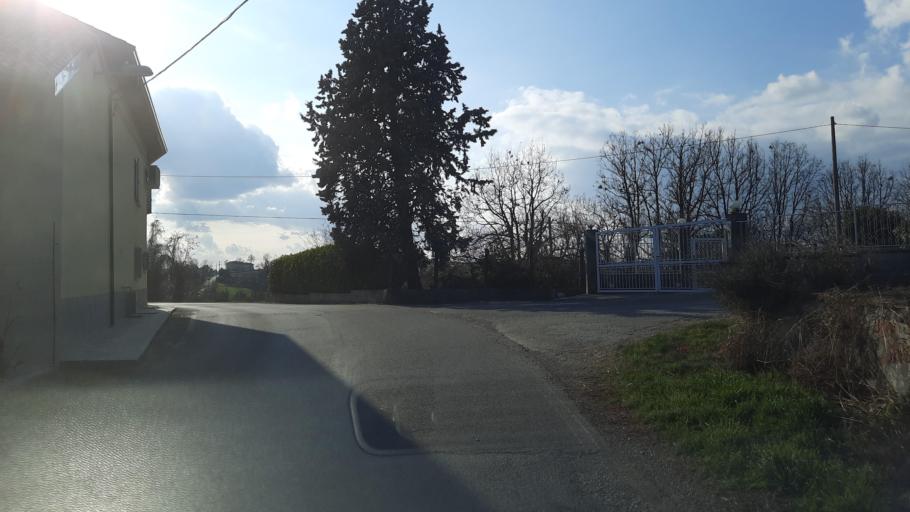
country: IT
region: Piedmont
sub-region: Provincia di Alessandria
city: San Giorgio
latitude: 45.1171
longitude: 8.4079
